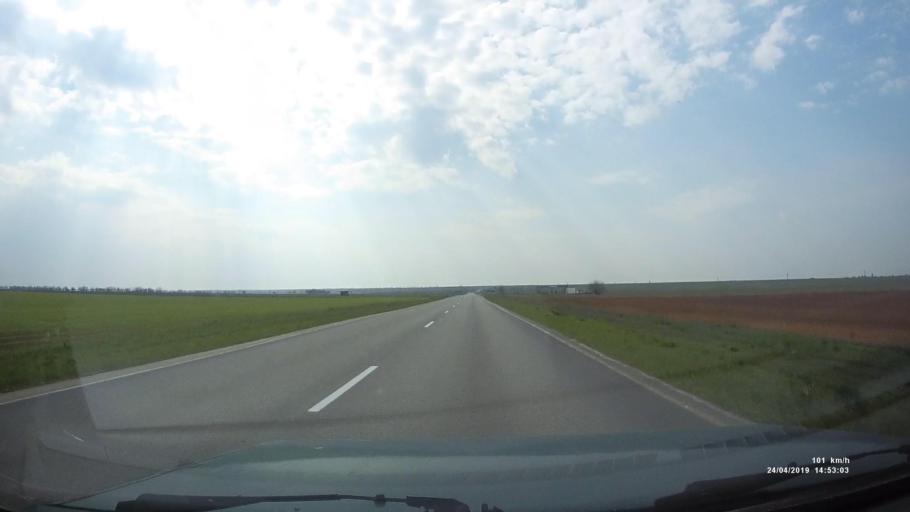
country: RU
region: Rostov
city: Remontnoye
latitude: 46.5309
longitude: 43.6673
